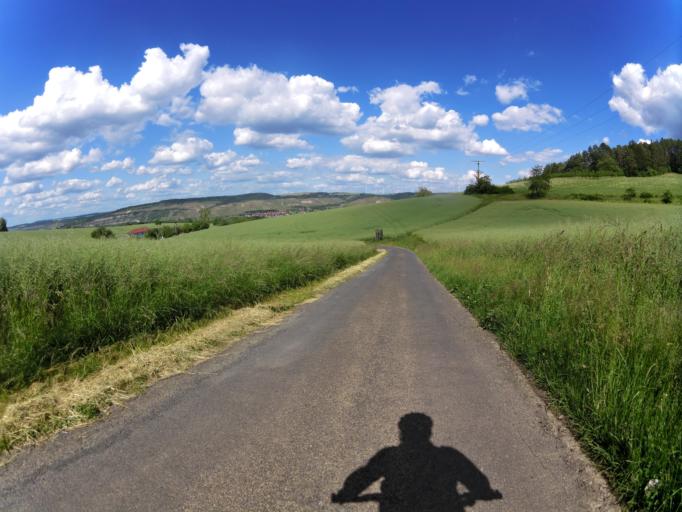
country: DE
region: Bavaria
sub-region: Regierungsbezirk Unterfranken
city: Erlabrunn
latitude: 49.8675
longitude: 9.8223
